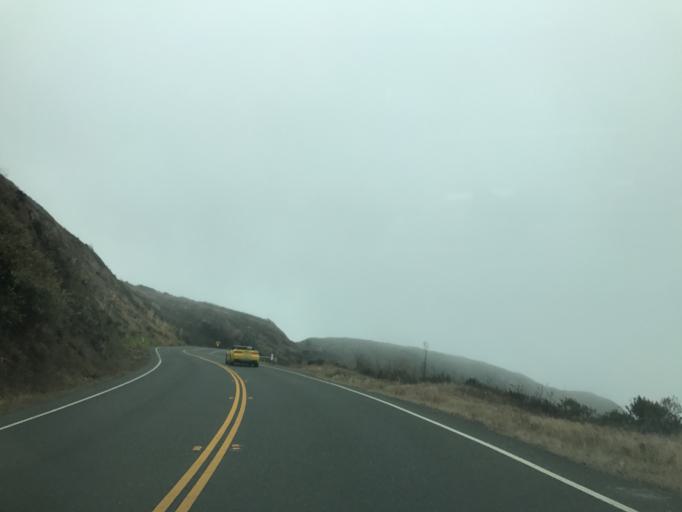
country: US
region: California
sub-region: Sonoma County
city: Monte Rio
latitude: 38.4688
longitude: -123.1538
